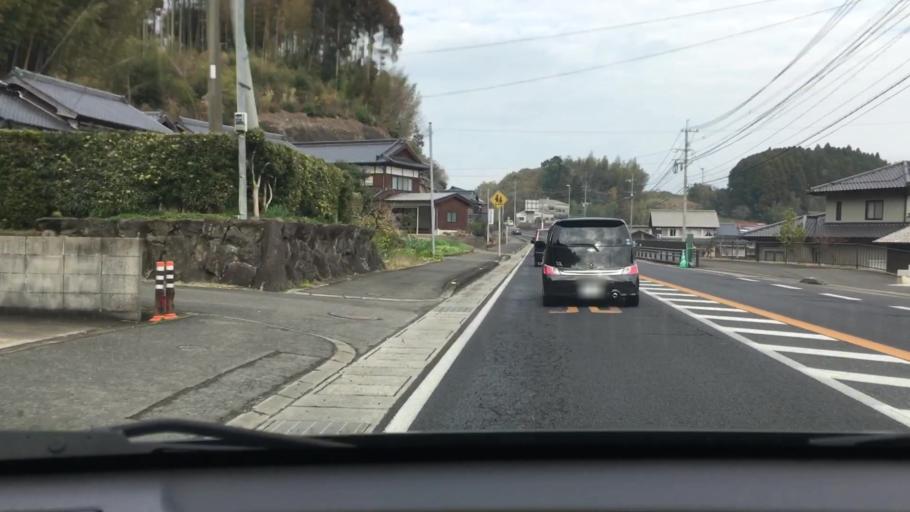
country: JP
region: Saga Prefecture
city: Imaricho-ko
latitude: 33.3076
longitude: 129.9266
